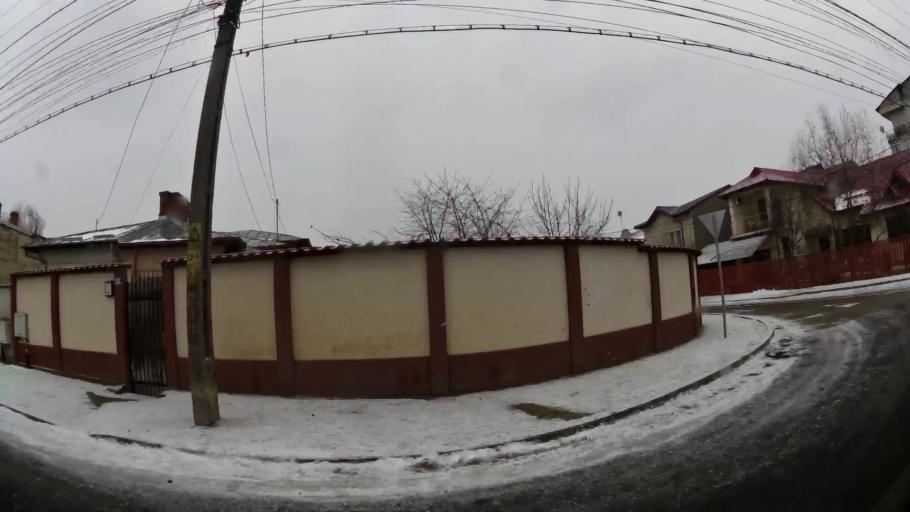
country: RO
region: Dambovita
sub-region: Municipiul Targoviste
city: Targoviste
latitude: 44.9352
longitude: 25.4486
